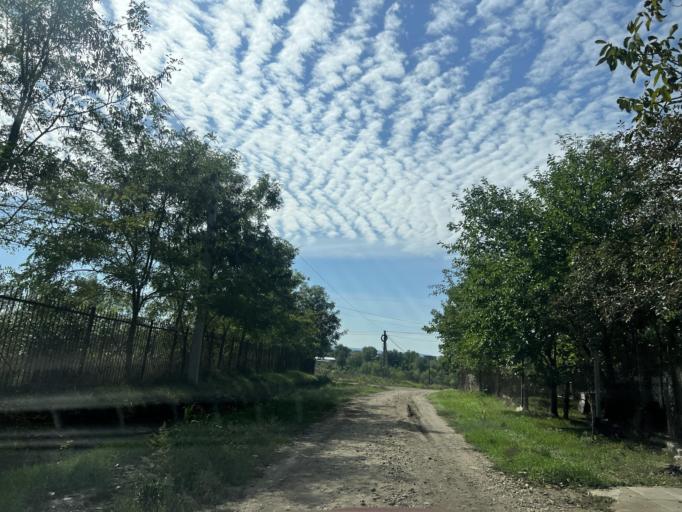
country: MD
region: Ungheni
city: Ungheni
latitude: 47.1979
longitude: 27.8152
